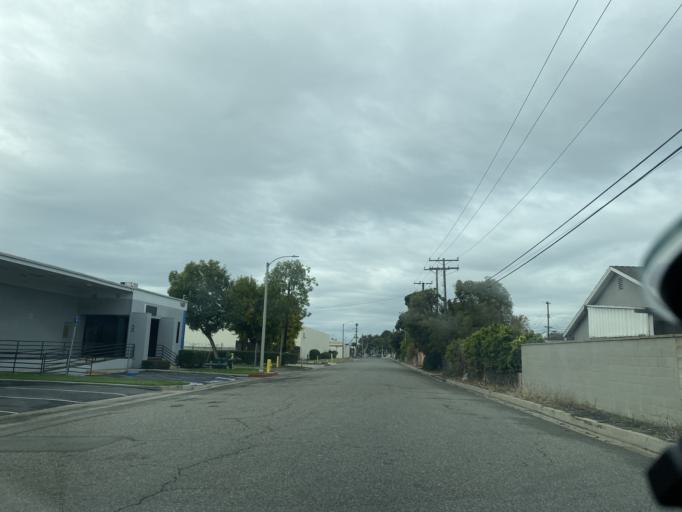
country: US
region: California
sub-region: Orange County
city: Fullerton
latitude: 33.8684
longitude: -117.9038
